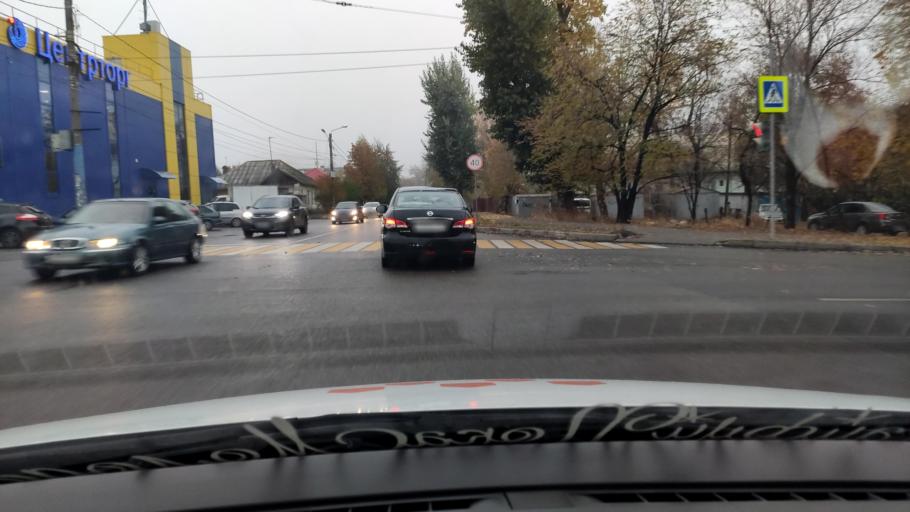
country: RU
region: Voronezj
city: Voronezh
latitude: 51.6972
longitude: 39.1642
